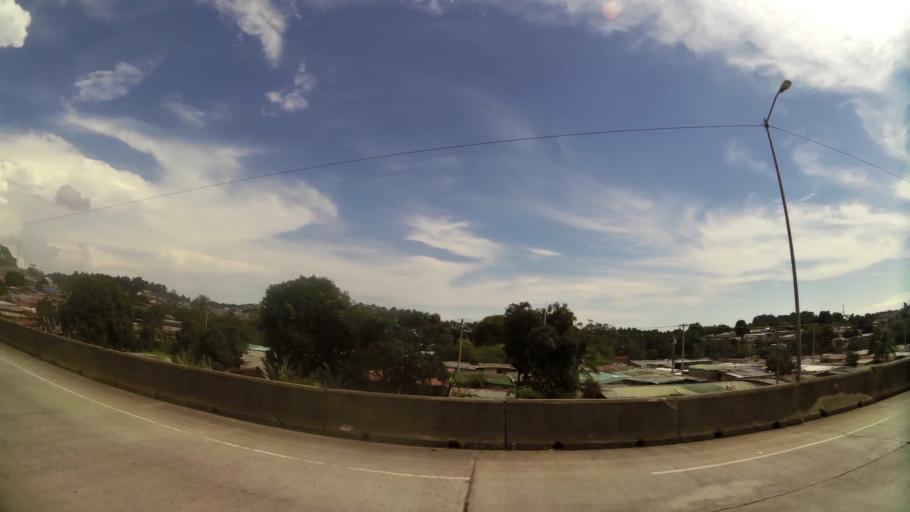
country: PA
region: Panama
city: San Miguelito
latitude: 9.0713
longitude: -79.4940
